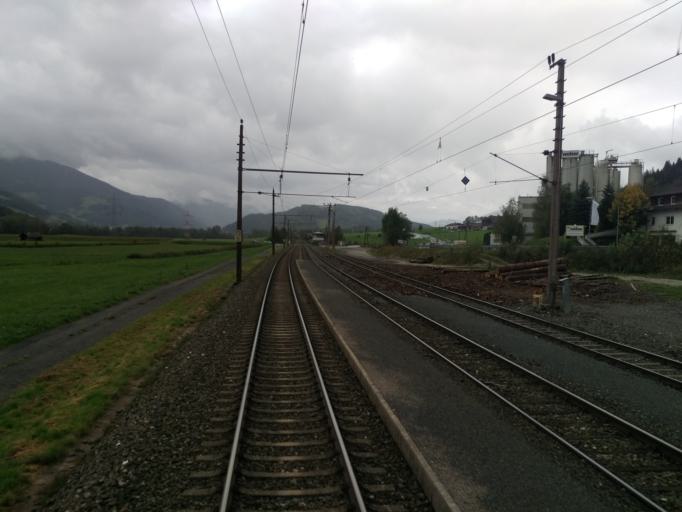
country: AT
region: Styria
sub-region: Politischer Bezirk Liezen
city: Niederoblarn
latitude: 47.4962
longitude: 14.0301
